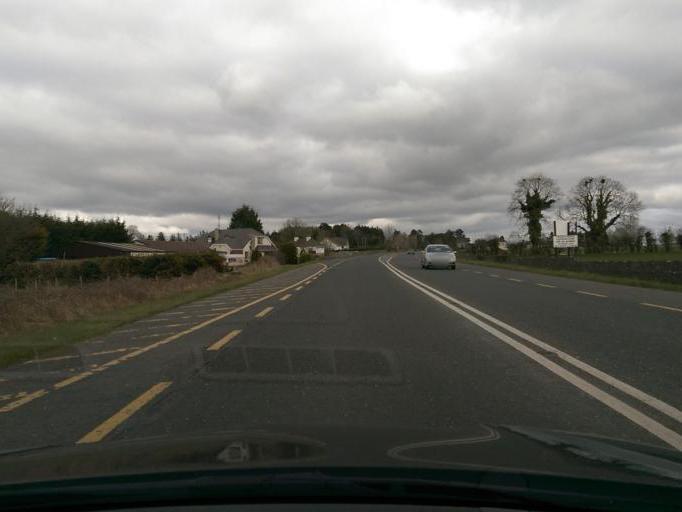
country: IE
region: Connaught
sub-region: County Galway
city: Ballinasloe
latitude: 53.3295
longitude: -8.1581
